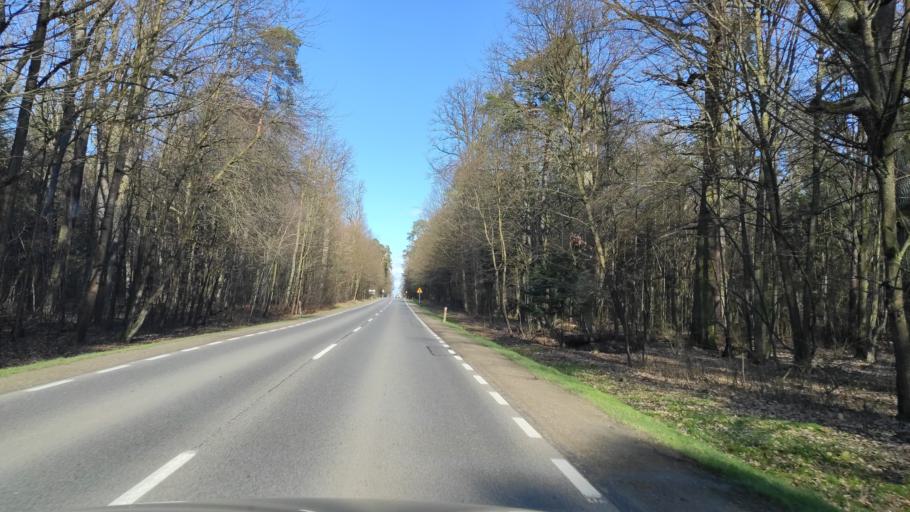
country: PL
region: Masovian Voivodeship
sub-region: Powiat radomski
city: Jedlnia-Letnisko
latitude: 51.4445
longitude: 21.3201
